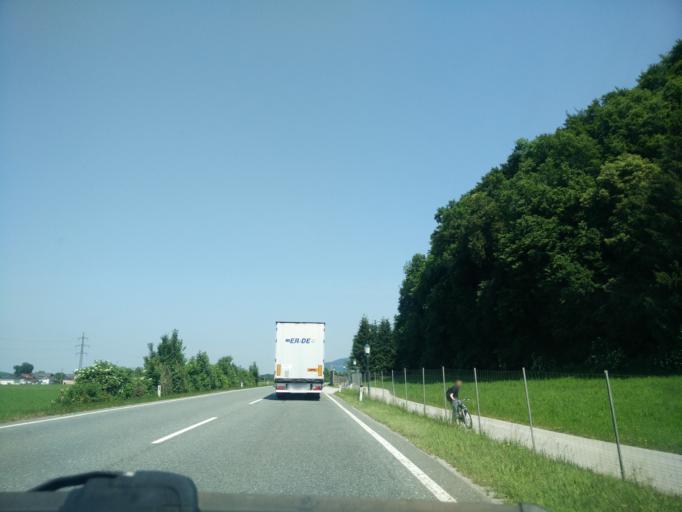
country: AT
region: Salzburg
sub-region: Politischer Bezirk Salzburg-Umgebung
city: Bergheim
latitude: 47.8558
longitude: 13.0180
